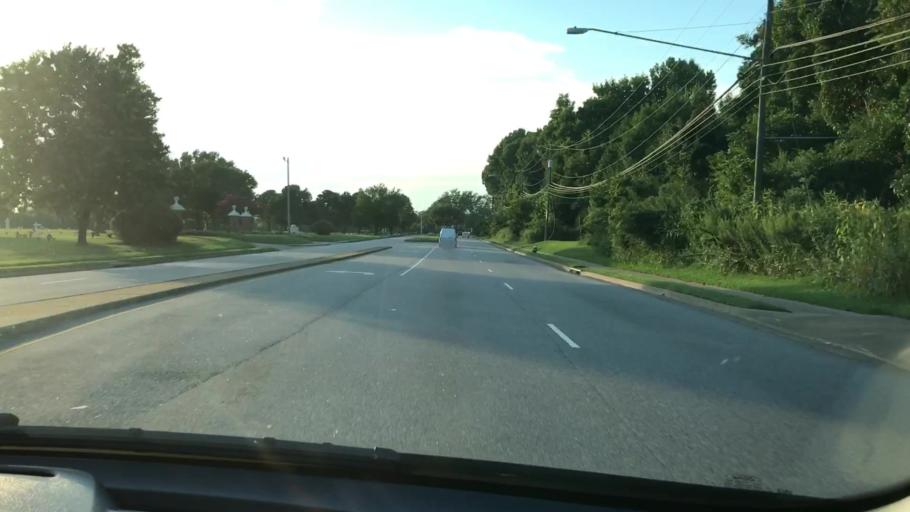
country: US
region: Virginia
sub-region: City of Hampton
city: Hampton
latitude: 37.0556
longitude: -76.3816
